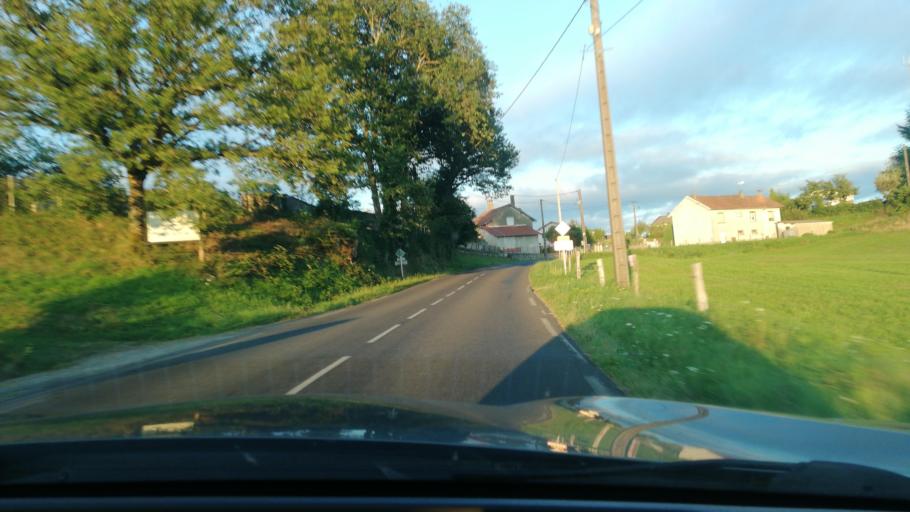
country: FR
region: Auvergne
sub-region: Departement du Cantal
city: Laroquebrou
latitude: 44.9574
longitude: 2.1218
